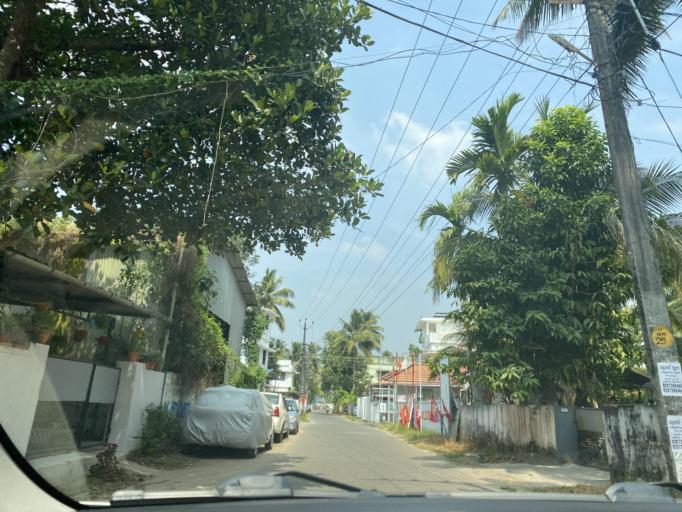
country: IN
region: Kerala
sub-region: Ernakulam
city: Cochin
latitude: 9.9403
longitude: 76.3076
